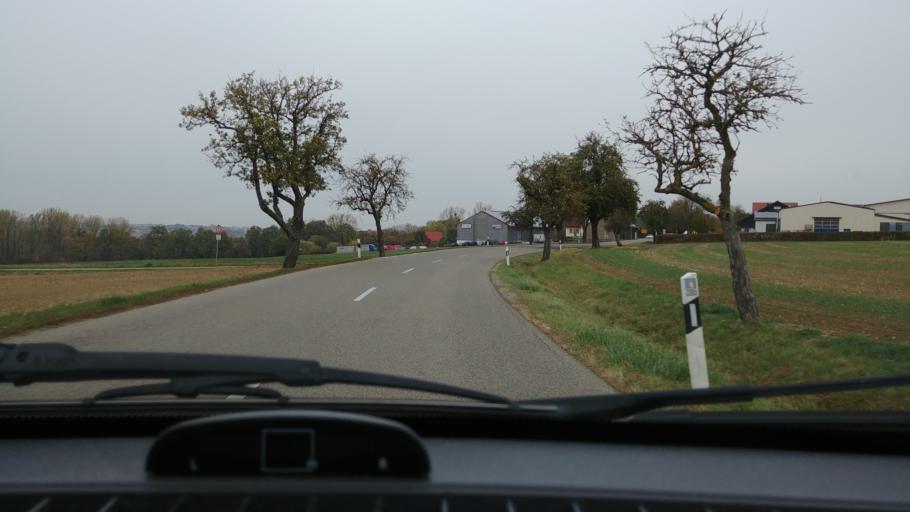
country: DE
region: Bavaria
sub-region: Regierungsbezirk Mittelfranken
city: Insingen
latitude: 49.3099
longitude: 10.0868
